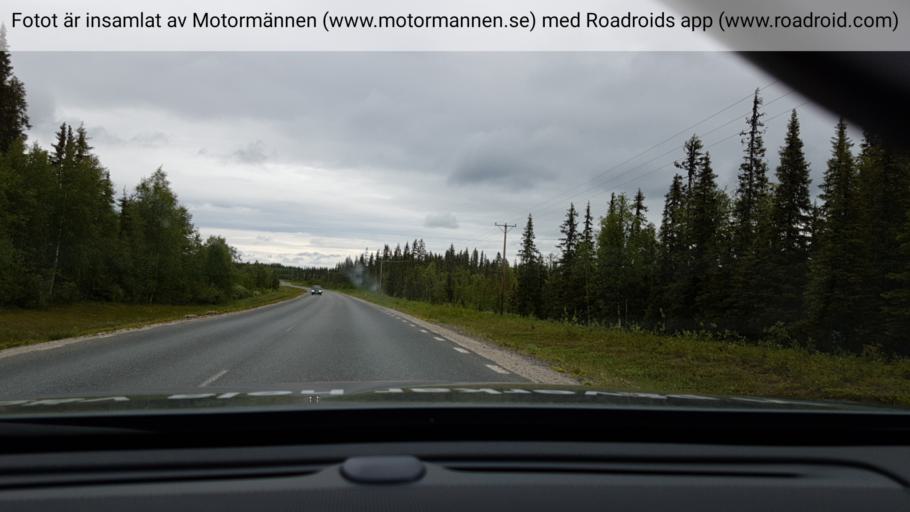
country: SE
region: Vaesterbotten
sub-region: Lycksele Kommun
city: Soderfors
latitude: 64.4413
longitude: 18.1184
